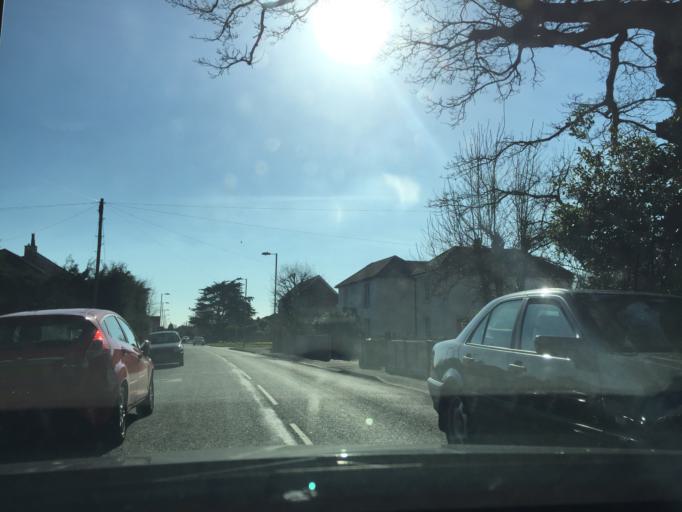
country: GB
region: England
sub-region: Hampshire
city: Hayling Island
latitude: 50.7988
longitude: -0.9833
